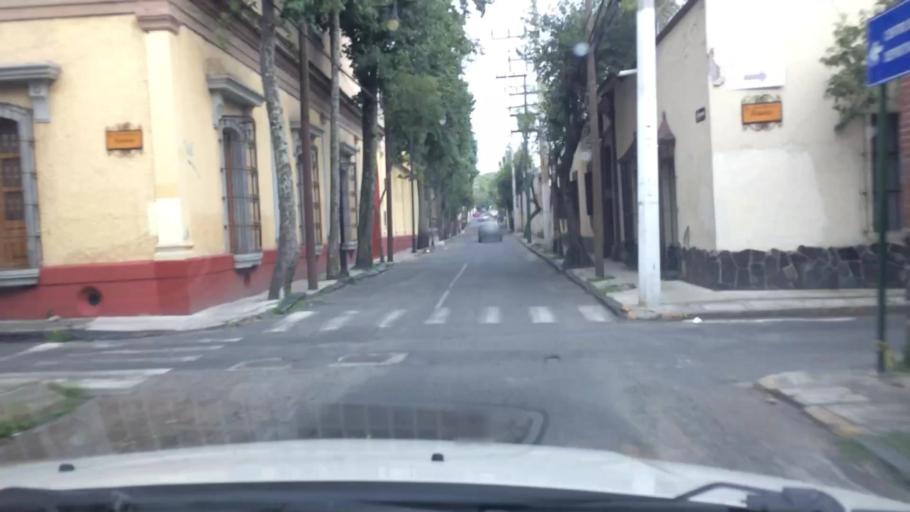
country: MX
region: Mexico City
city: Tlalpan
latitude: 19.2901
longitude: -99.1702
